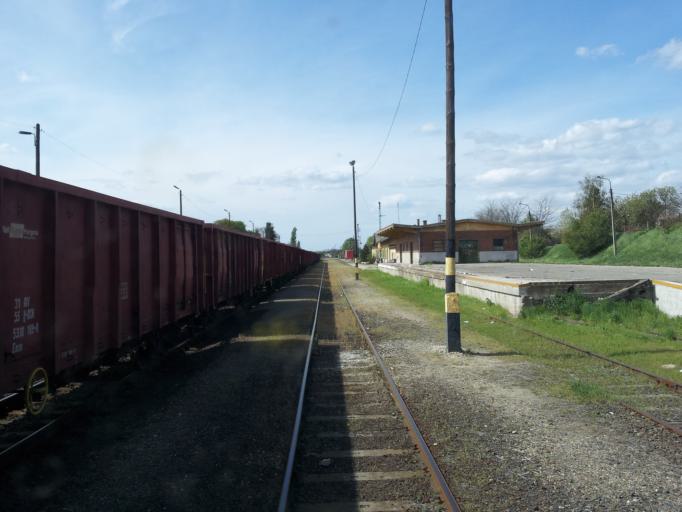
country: HU
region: Fejer
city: Mor
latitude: 47.3685
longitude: 18.1898
